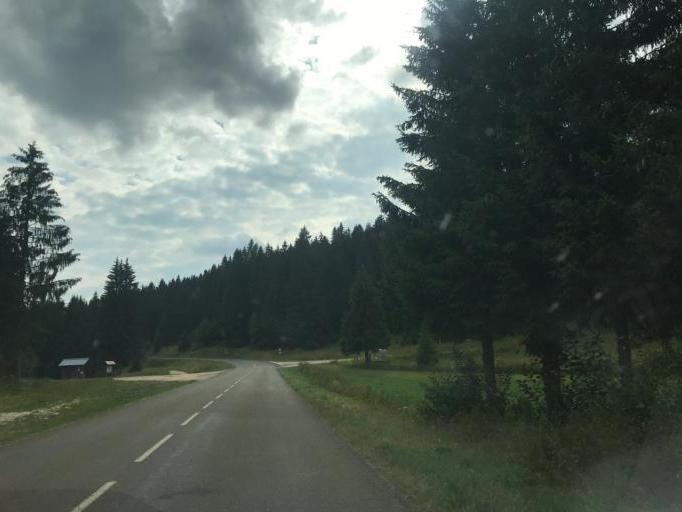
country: FR
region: Franche-Comte
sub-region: Departement du Jura
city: Valfin-les-Saint-Claude
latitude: 46.4979
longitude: 5.8553
